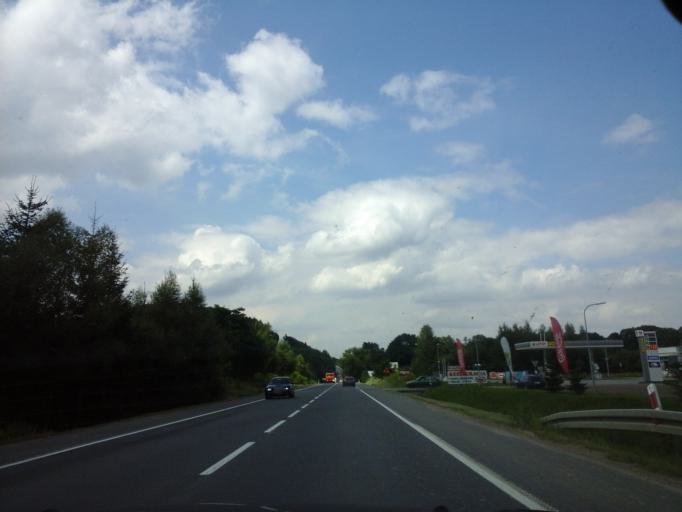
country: PL
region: Lesser Poland Voivodeship
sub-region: Powiat wadowicki
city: Jaroszowice
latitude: 49.8055
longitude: 19.5446
